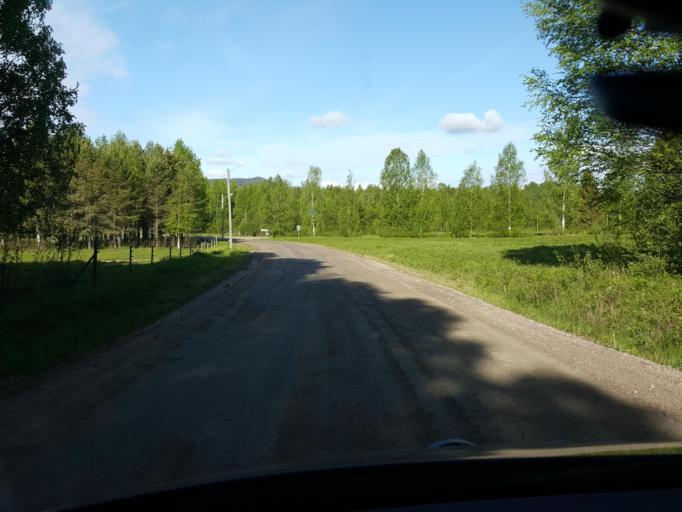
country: SE
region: Vaesternorrland
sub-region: Ange Kommun
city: Ange
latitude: 62.1838
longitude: 15.6411
